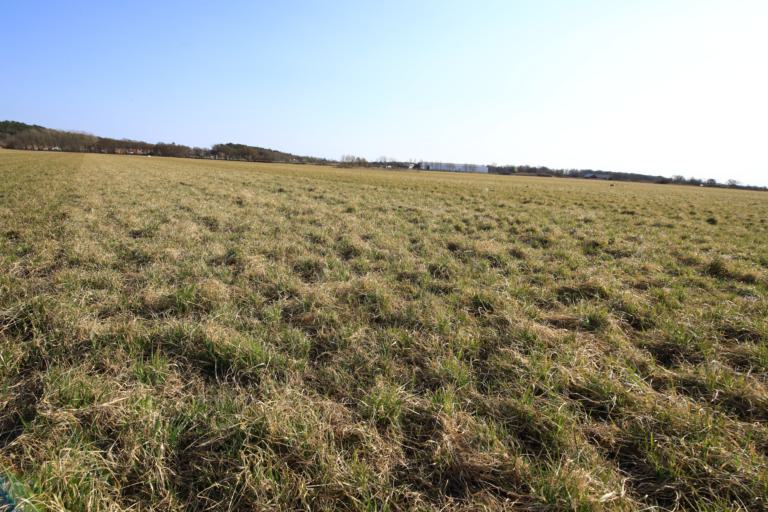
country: SE
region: Halland
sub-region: Varbergs Kommun
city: Varberg
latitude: 57.1435
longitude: 12.2760
